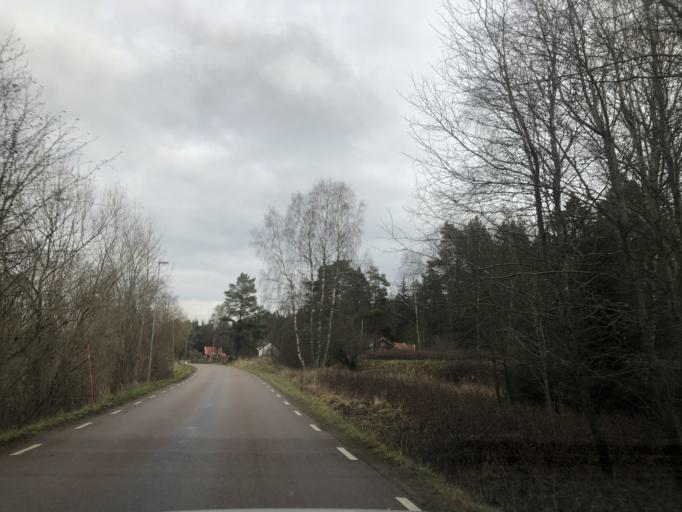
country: SE
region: Vaestra Goetaland
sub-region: Boras Kommun
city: Dalsjofors
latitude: 57.8195
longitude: 13.1509
